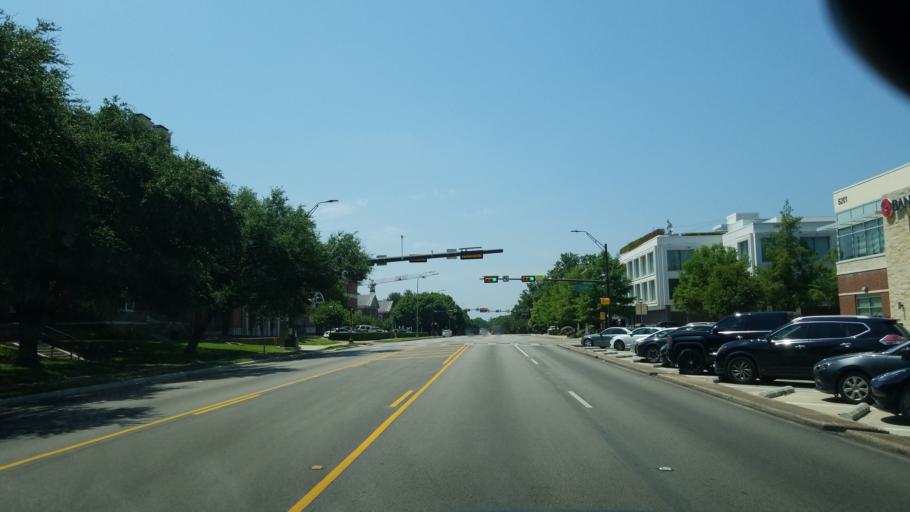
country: US
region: Texas
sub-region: Dallas County
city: Highland Park
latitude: 32.8423
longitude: -96.7871
